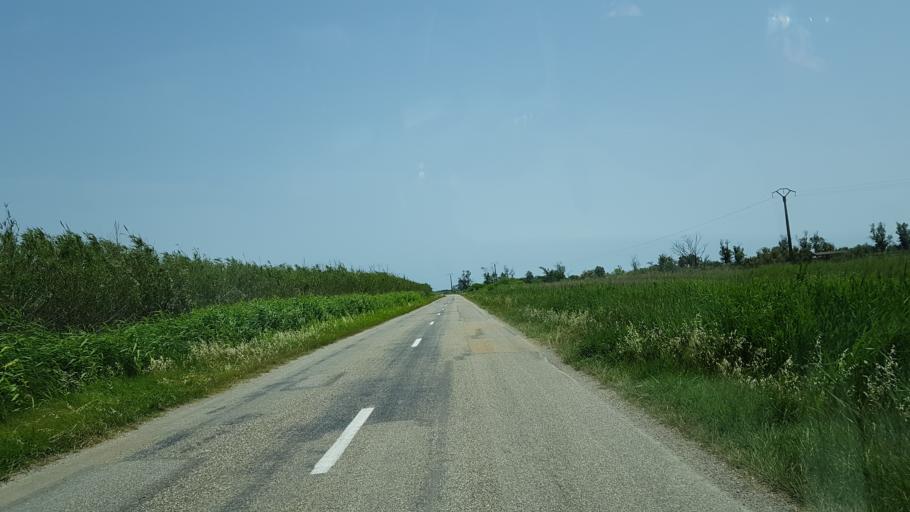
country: FR
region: Provence-Alpes-Cote d'Azur
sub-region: Departement des Bouches-du-Rhone
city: Port-Saint-Louis-du-Rhone
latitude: 43.4463
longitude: 4.6641
